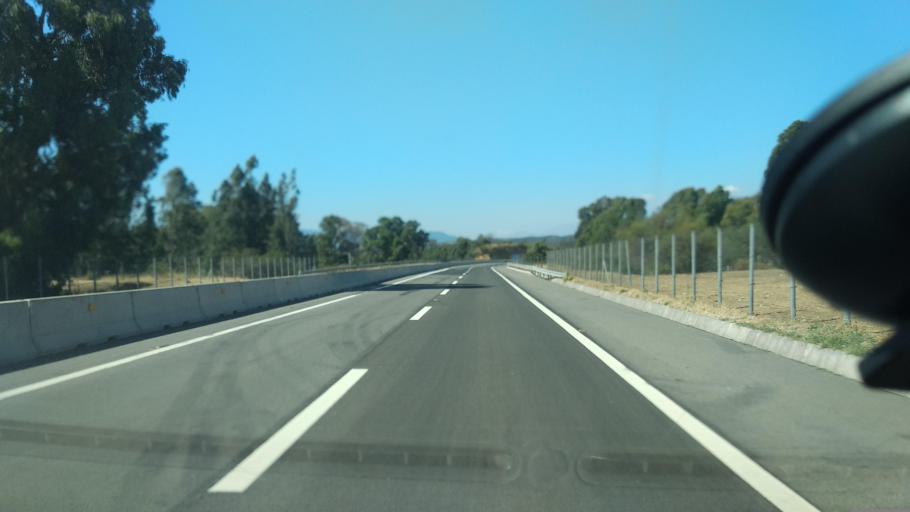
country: CL
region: Valparaiso
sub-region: Provincia de Marga Marga
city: Limache
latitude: -32.9913
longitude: -71.3280
